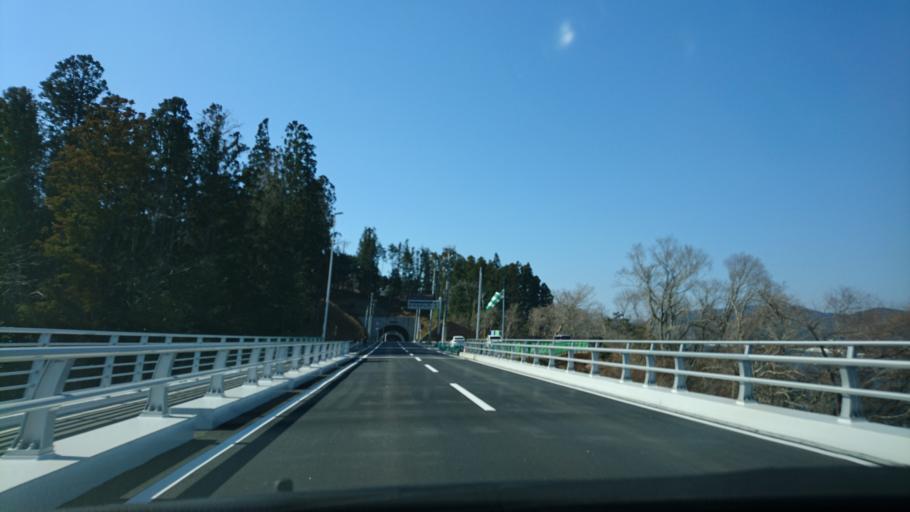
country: JP
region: Iwate
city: Ofunato
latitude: 38.8776
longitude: 141.6056
